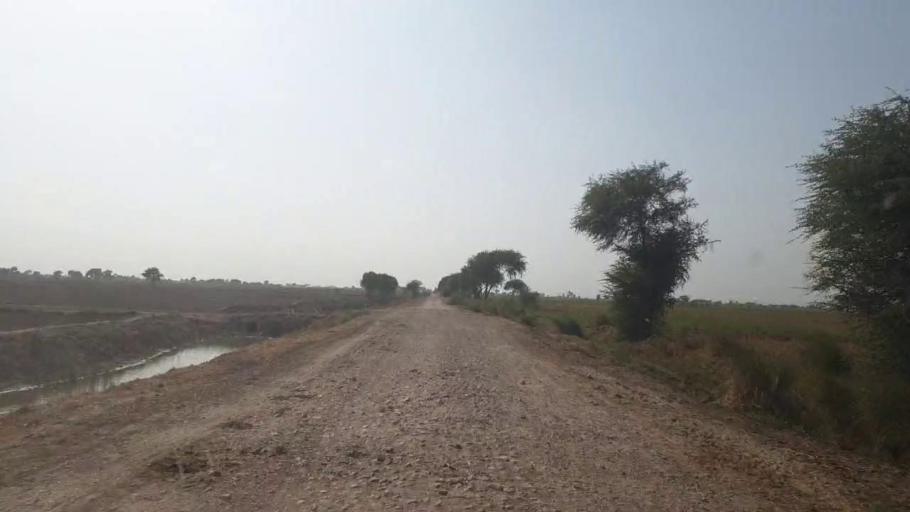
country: PK
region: Sindh
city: Kario
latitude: 24.5589
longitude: 68.5149
